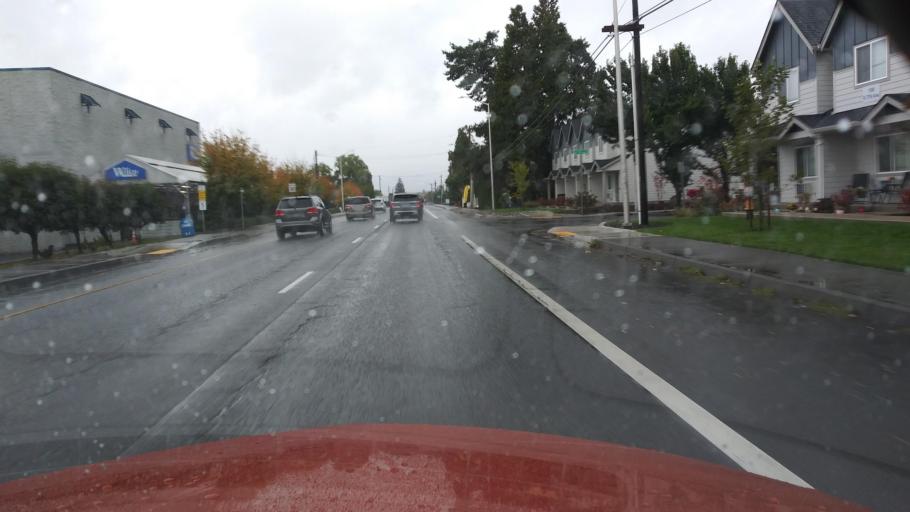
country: US
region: Oregon
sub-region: Washington County
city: Cornelius
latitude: 45.5210
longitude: -123.0622
